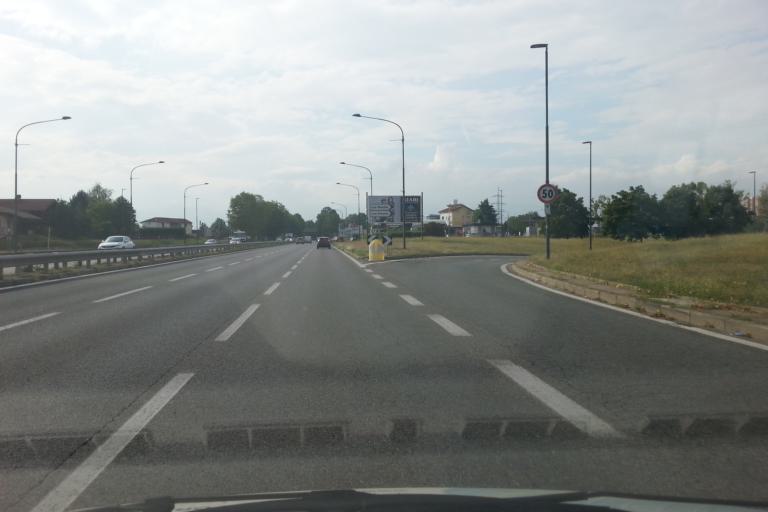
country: IT
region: Piedmont
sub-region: Provincia di Torino
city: Savonera
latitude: 45.0975
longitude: 7.6227
